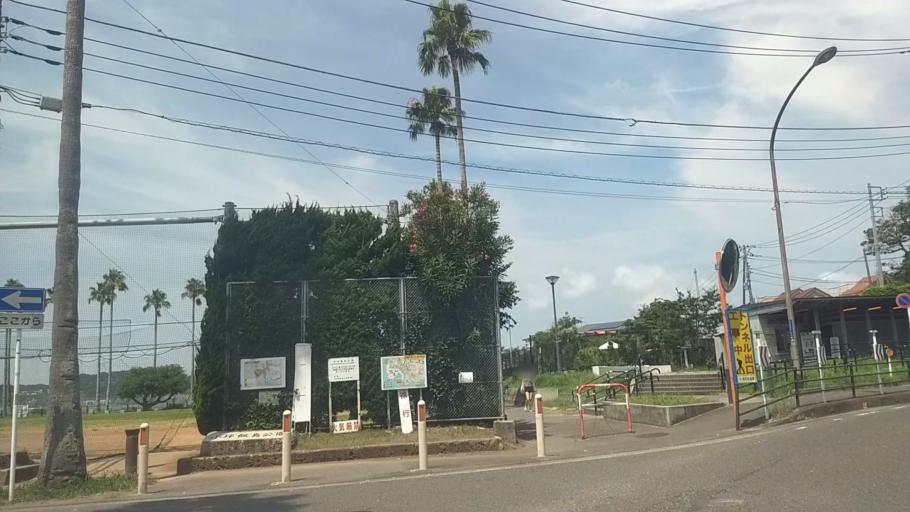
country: JP
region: Kanagawa
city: Kamakura
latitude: 35.2984
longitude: 139.5532
